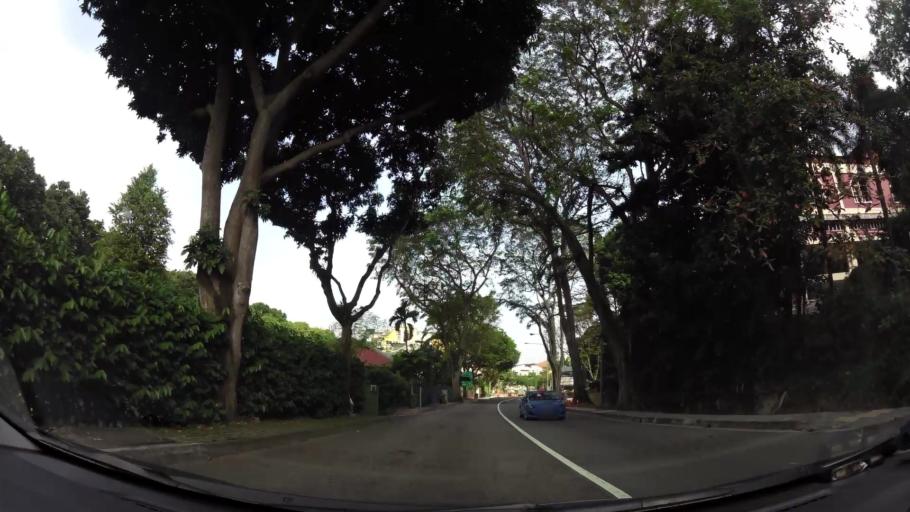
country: SG
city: Singapore
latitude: 1.2869
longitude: 103.7794
